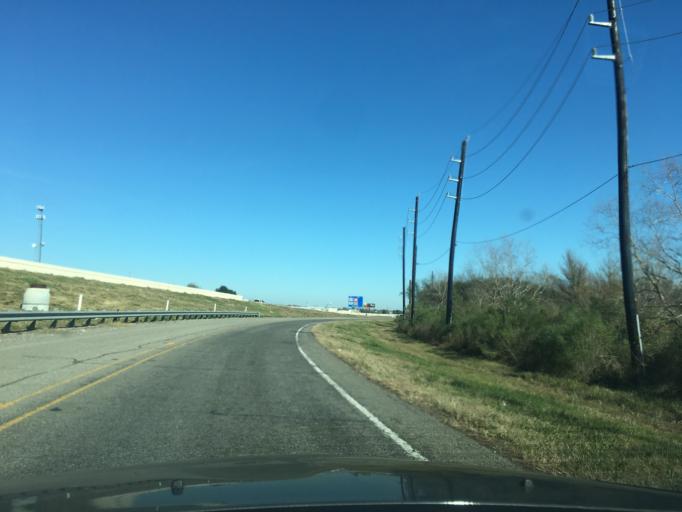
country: US
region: Texas
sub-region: Fort Bend County
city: Pleak
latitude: 29.4845
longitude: -95.9351
